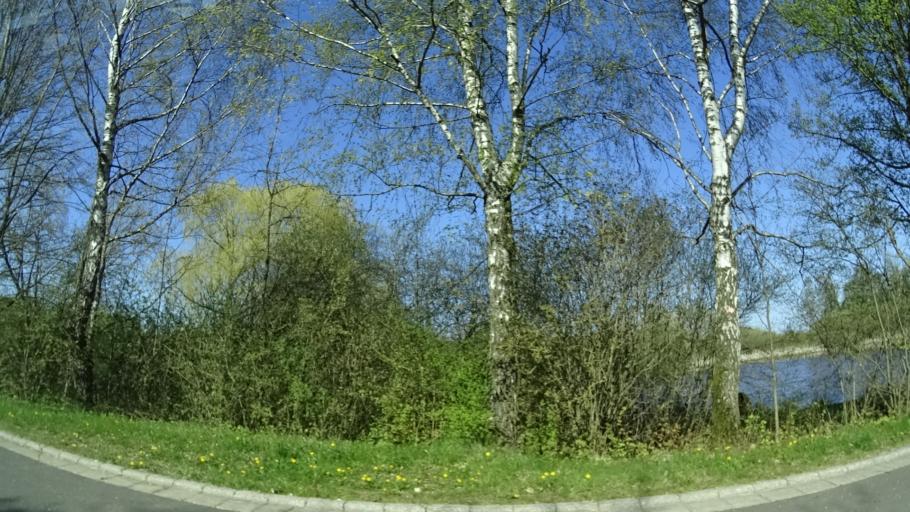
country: DE
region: Bavaria
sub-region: Upper Palatinate
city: Edelsfeld
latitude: 49.5442
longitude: 11.7195
